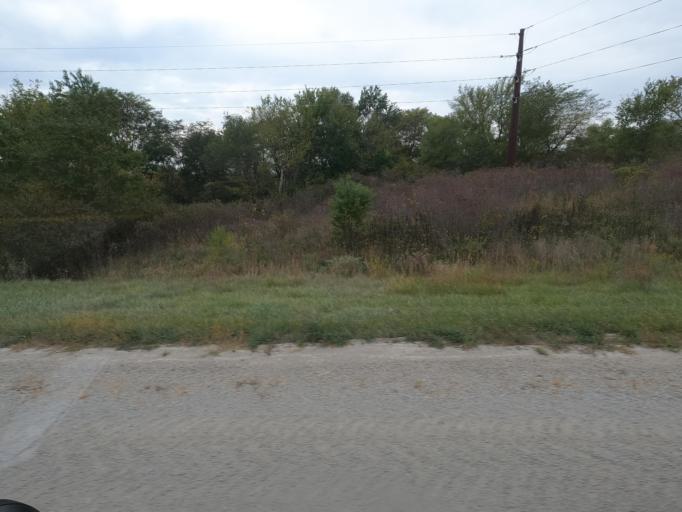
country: US
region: Iowa
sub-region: Marion County
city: Pella
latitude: 41.4034
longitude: -92.9398
